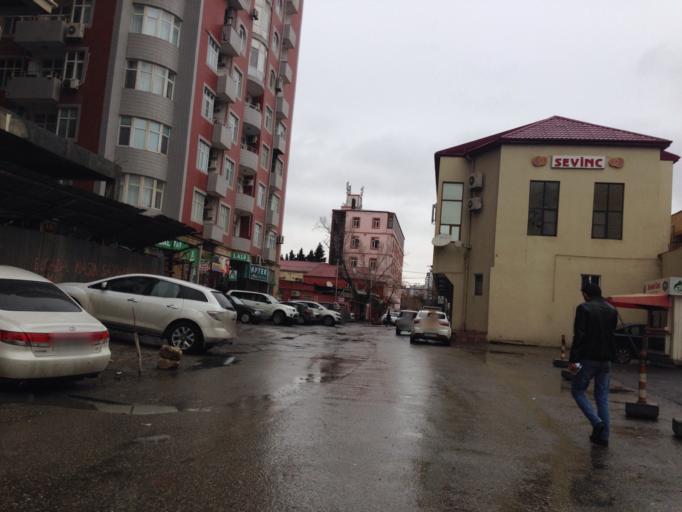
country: AZ
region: Baki
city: Baku
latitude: 40.3811
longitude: 49.8627
